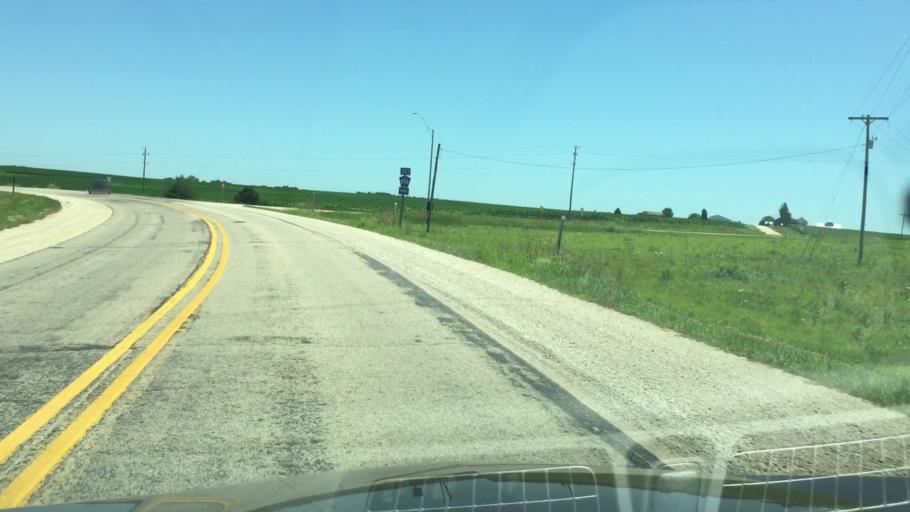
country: US
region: Iowa
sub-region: Cedar County
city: Mechanicsville
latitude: 41.9617
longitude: -91.1441
